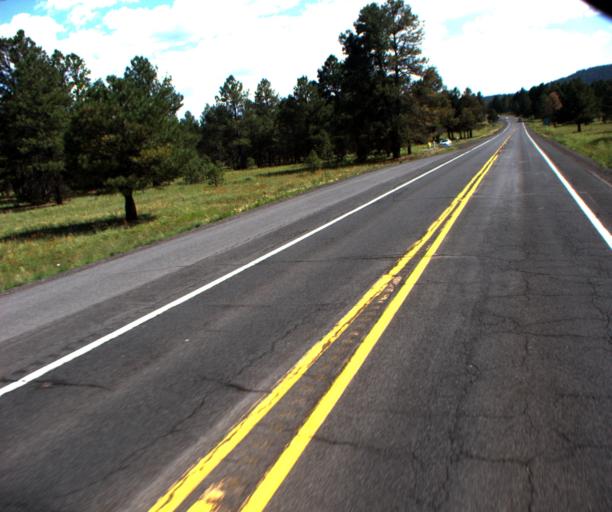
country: US
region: Arizona
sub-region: Coconino County
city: Williams
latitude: 35.2698
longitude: -112.1492
